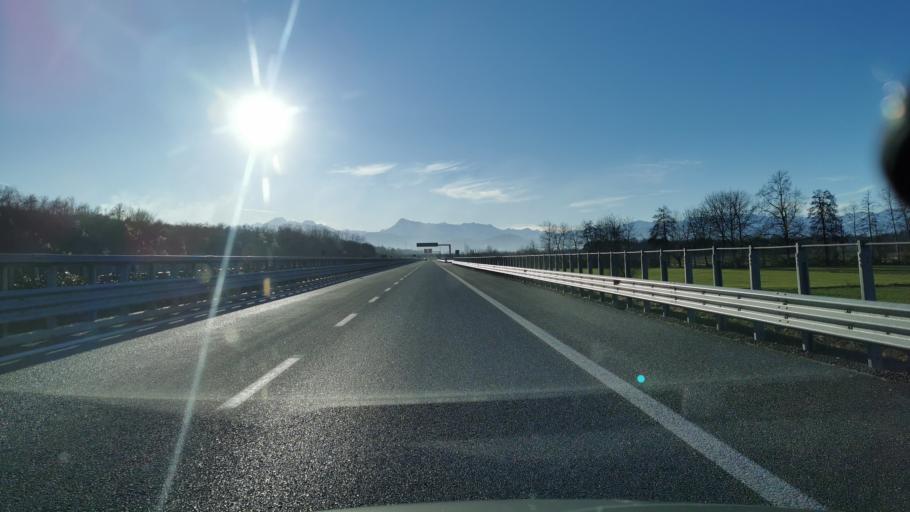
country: IT
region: Piedmont
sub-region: Provincia di Cuneo
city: Castelletto Stura
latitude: 44.4385
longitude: 7.6220
